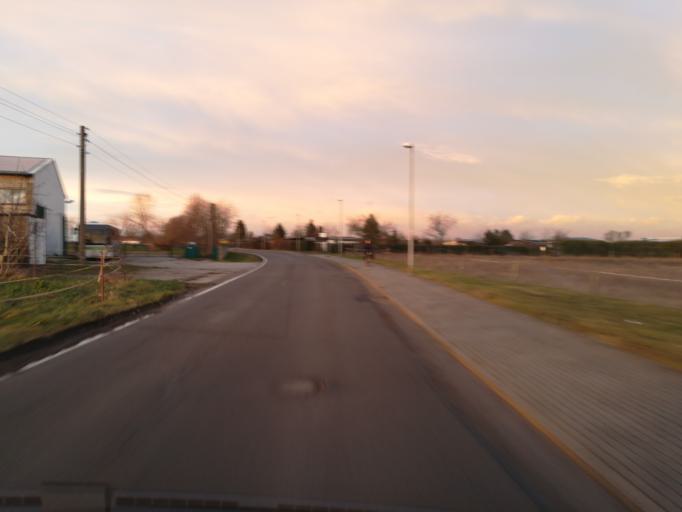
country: DE
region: Saxony
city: Wiedemar
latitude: 51.5005
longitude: 12.2279
